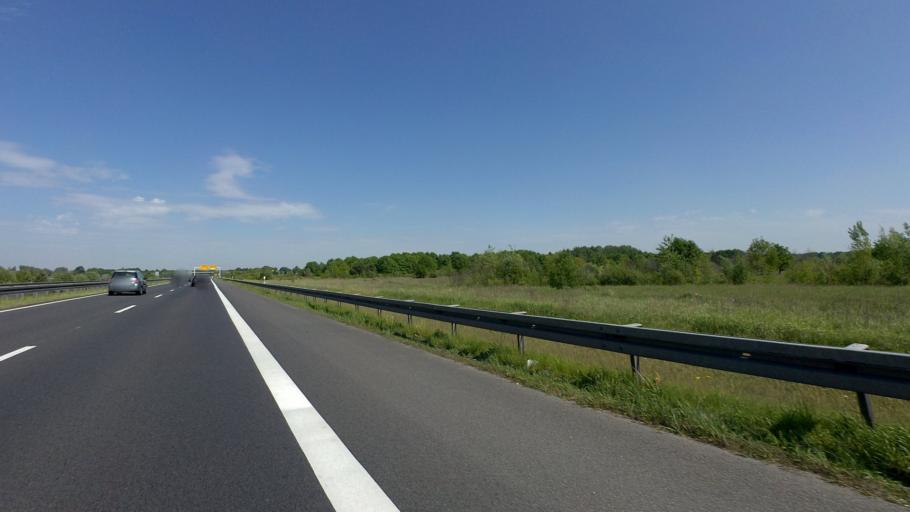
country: DE
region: Brandenburg
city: Leegebruch
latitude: 52.7329
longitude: 13.2117
